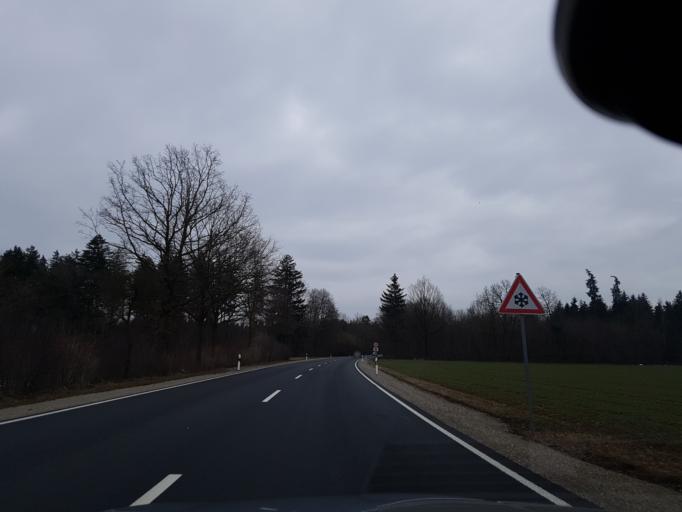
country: DE
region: Bavaria
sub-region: Upper Bavaria
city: Hohenkirchen-Siegertsbrunn
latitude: 47.9843
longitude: 11.7230
